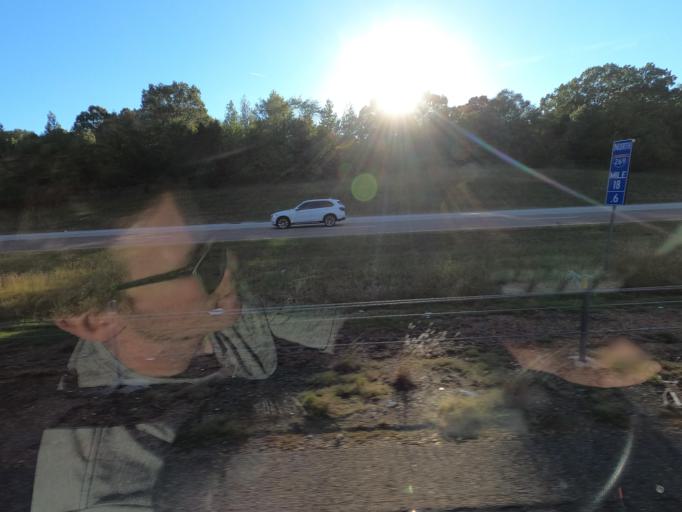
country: US
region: Tennessee
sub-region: Shelby County
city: Arlington
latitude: 35.2504
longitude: -89.6722
